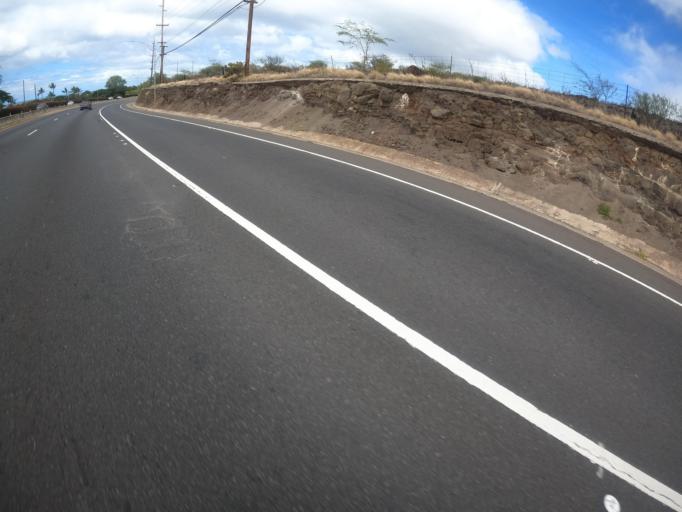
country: US
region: Hawaii
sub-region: Honolulu County
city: Makakilo City
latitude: 21.3443
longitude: -158.1185
